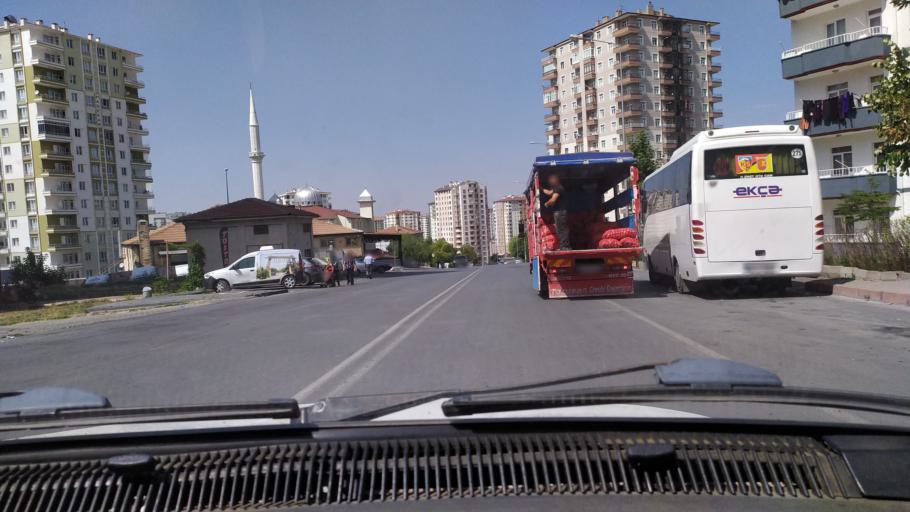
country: TR
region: Kayseri
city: Talas
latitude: 38.7057
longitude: 35.5614
